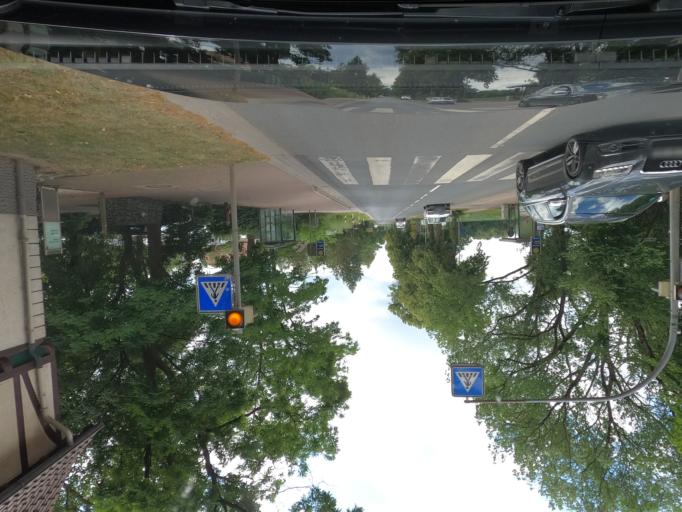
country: DE
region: Lower Saxony
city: Sehnde
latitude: 52.3335
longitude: 9.9451
